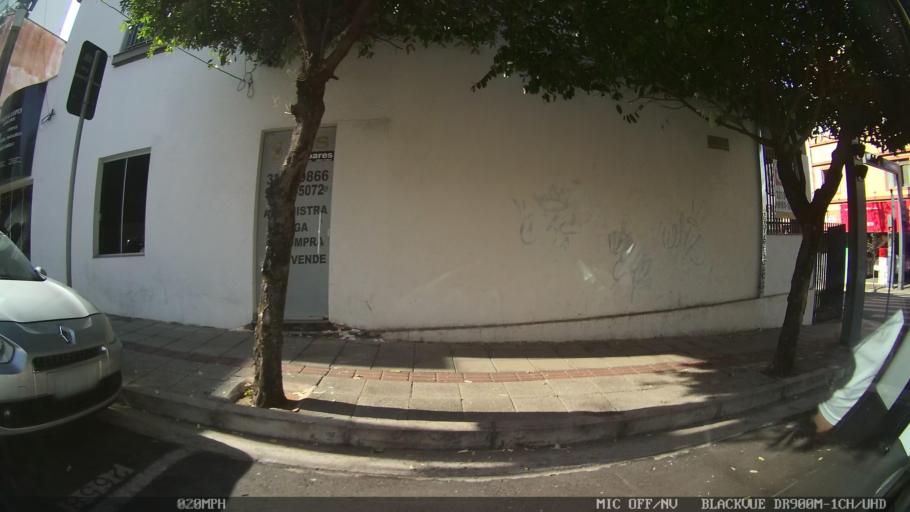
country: BR
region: Sao Paulo
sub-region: Sao Jose Do Rio Preto
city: Sao Jose do Rio Preto
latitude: -20.8166
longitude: -49.3833
